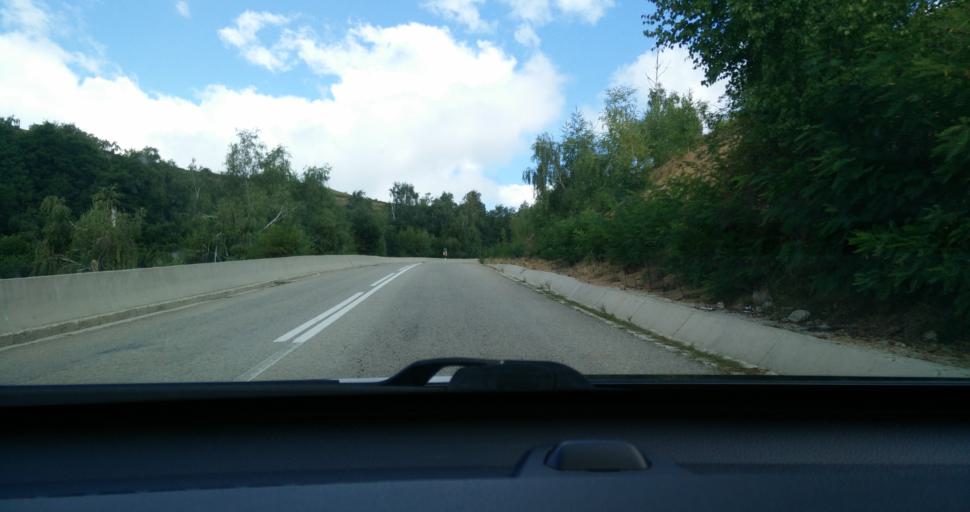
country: RO
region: Gorj
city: Novaci-Straini
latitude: 45.2134
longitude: 23.6979
